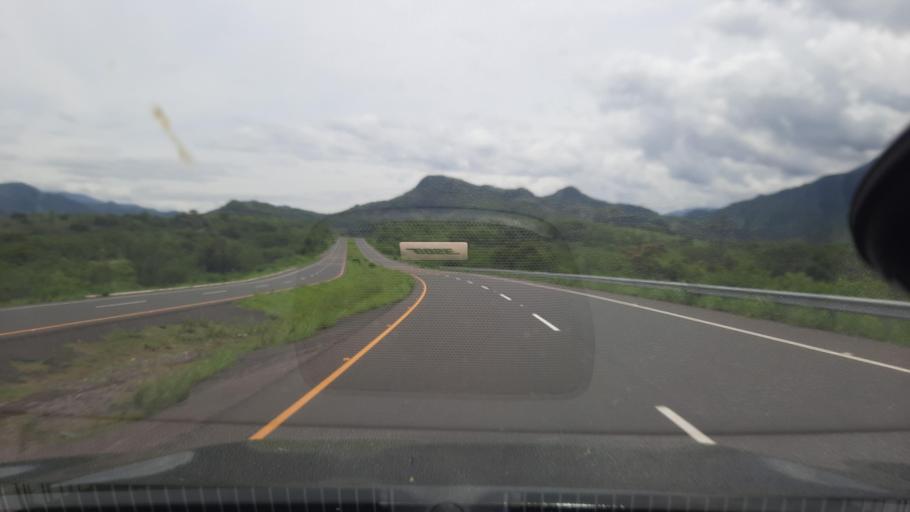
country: HN
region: Valle
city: Aramecina
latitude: 13.7754
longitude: -87.6996
